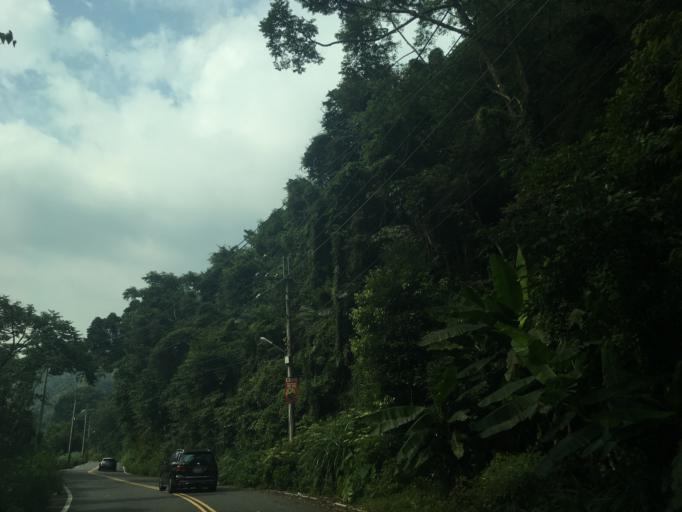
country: TW
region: Taiwan
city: Fengyuan
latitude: 24.3007
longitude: 120.9237
